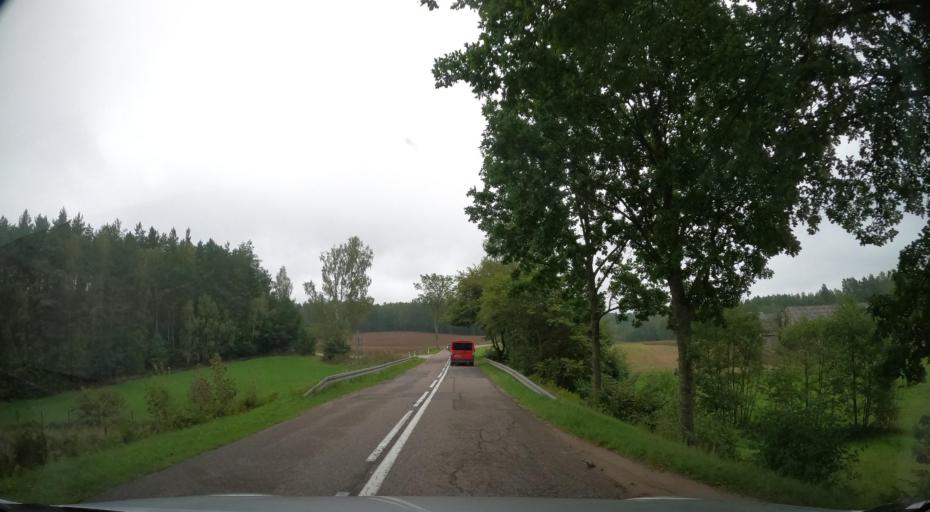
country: PL
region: Pomeranian Voivodeship
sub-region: Powiat wejherowski
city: Luzino
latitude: 54.4908
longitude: 18.1222
